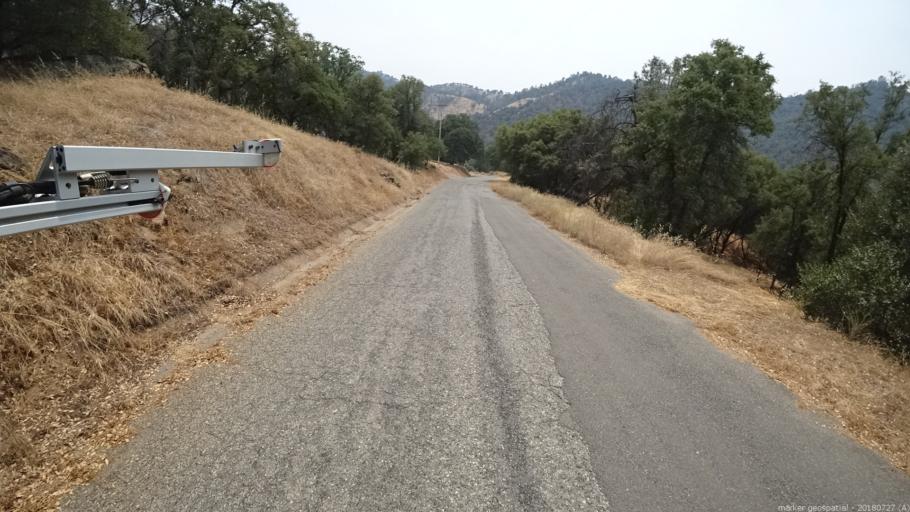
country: US
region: California
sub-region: Madera County
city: Coarsegold
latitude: 37.2665
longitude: -119.6852
